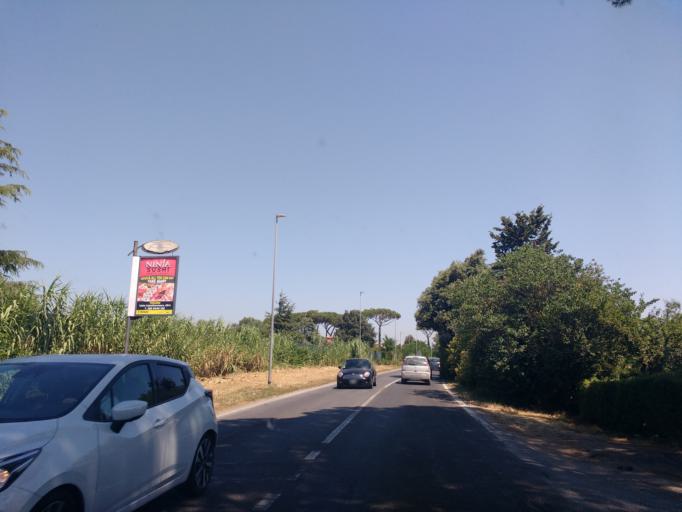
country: IT
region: Latium
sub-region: Citta metropolitana di Roma Capitale
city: Maccarese
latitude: 41.8708
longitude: 12.2086
